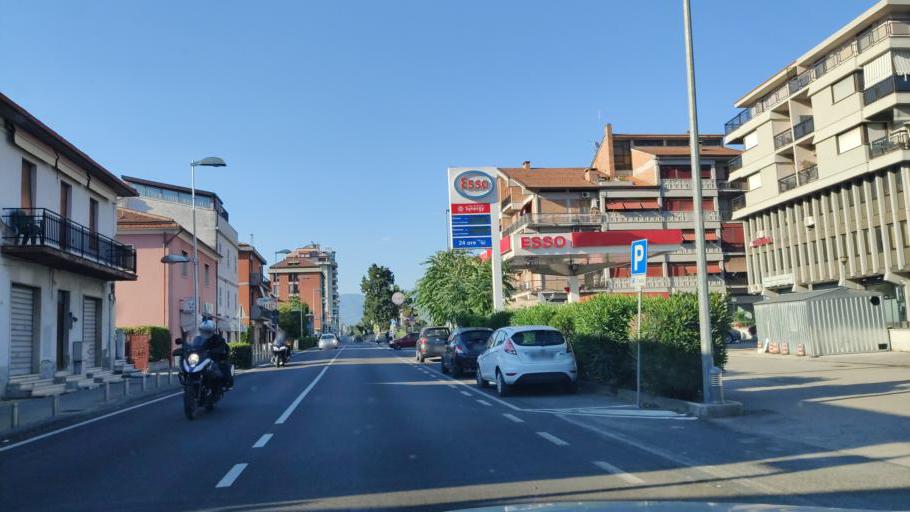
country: IT
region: Umbria
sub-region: Provincia di Terni
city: Narni Scalo
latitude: 42.5324
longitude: 12.5179
